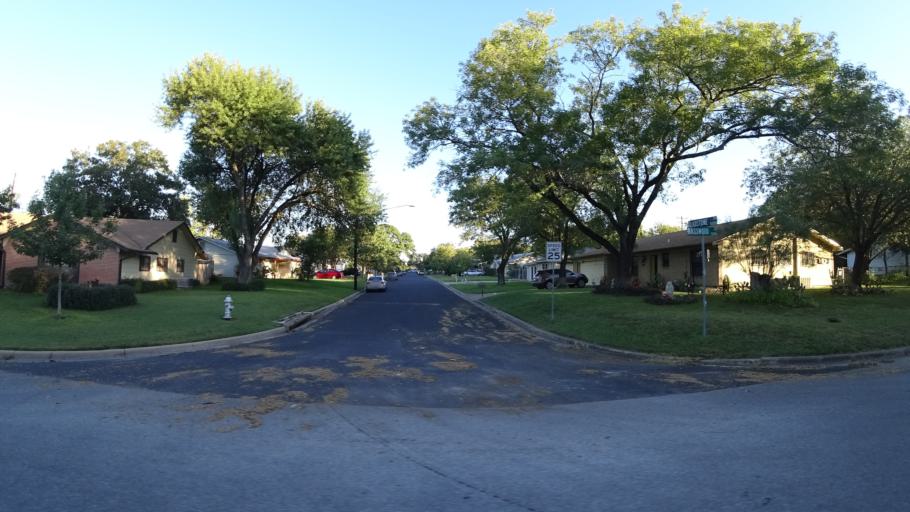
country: US
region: Texas
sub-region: Travis County
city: Austin
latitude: 30.2951
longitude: -97.6784
